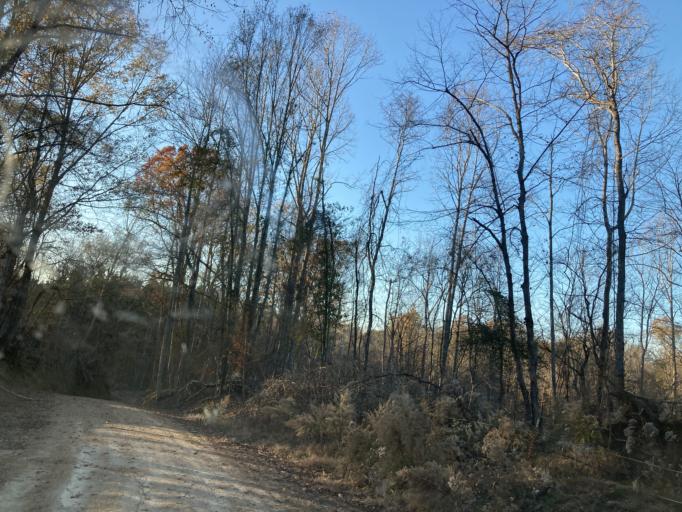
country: US
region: Mississippi
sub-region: Yazoo County
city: Yazoo City
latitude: 32.9469
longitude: -90.2849
